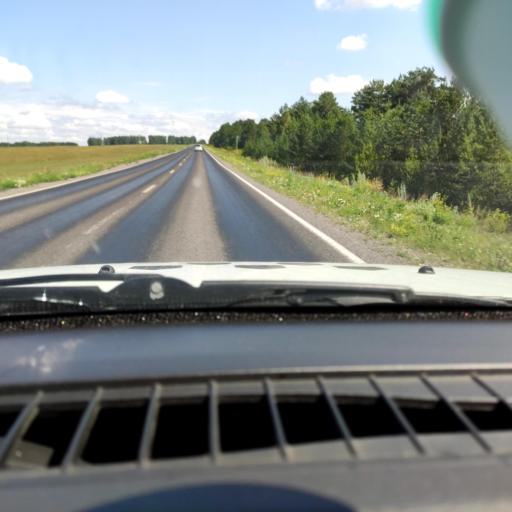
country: RU
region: Bashkortostan
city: Verkhniye Kigi
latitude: 55.4590
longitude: 58.4351
